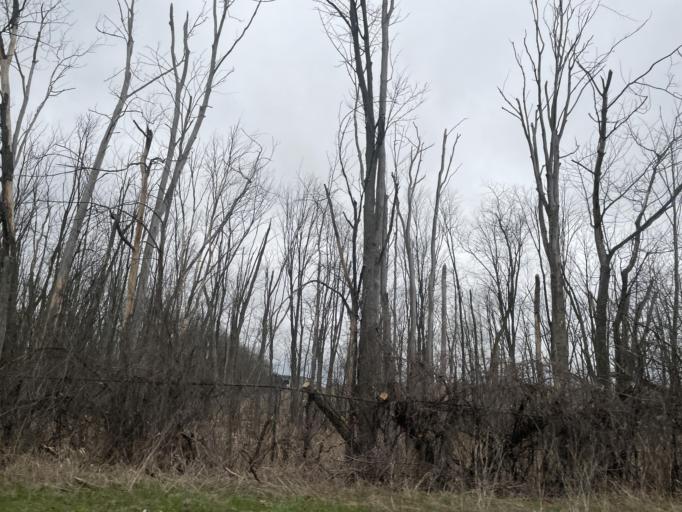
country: CA
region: Ontario
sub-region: Wellington County
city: Guelph
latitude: 43.5787
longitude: -80.2252
